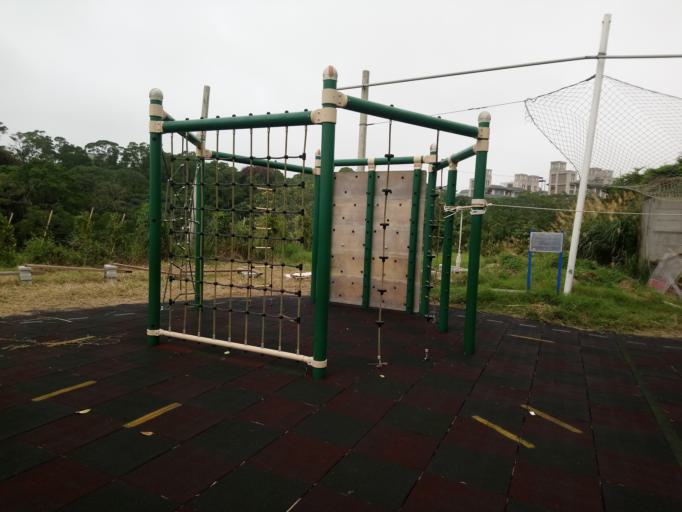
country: TW
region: Taiwan
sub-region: Hsinchu
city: Hsinchu
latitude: 24.7806
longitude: 120.9831
